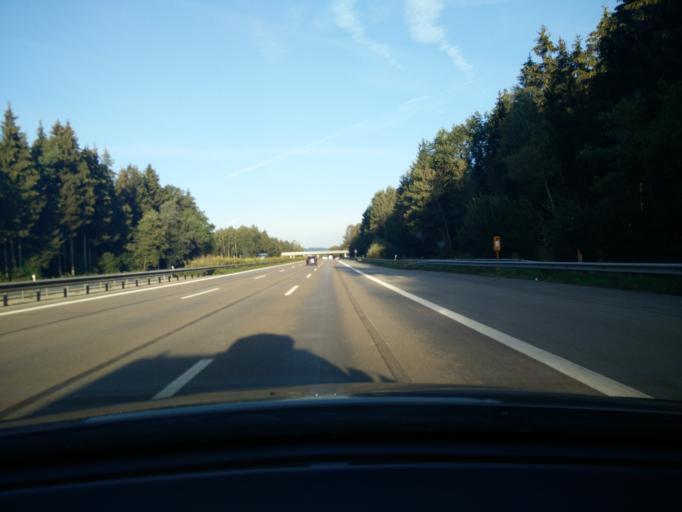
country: DE
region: Bavaria
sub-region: Upper Bavaria
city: Kolbermoor
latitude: 47.8136
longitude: 12.0724
